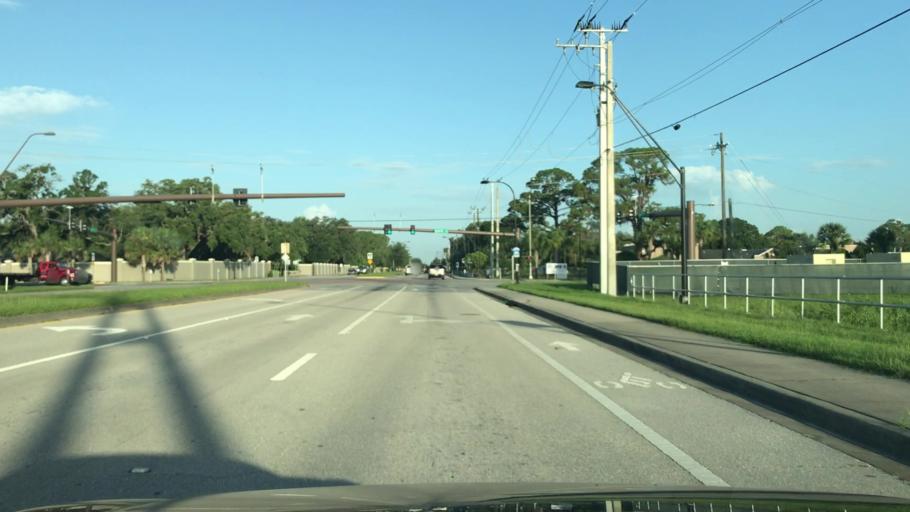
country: US
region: Florida
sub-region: Sarasota County
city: Fruitville
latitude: 27.3232
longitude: -82.4630
